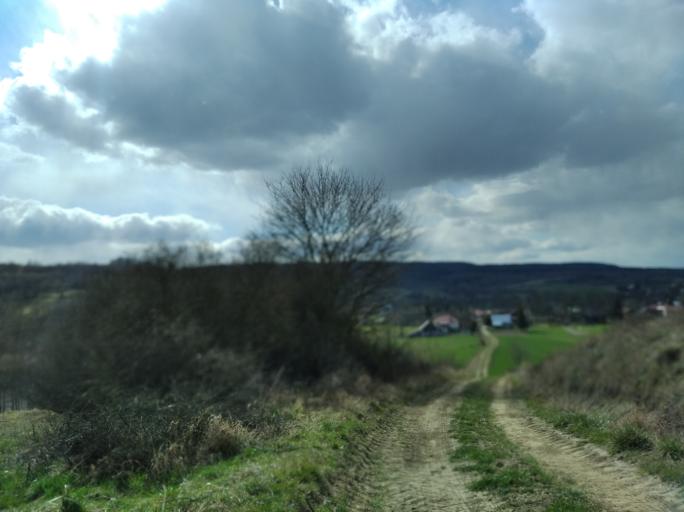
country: PL
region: Subcarpathian Voivodeship
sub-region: Powiat strzyzowski
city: Jawornik
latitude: 49.8341
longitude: 21.8431
